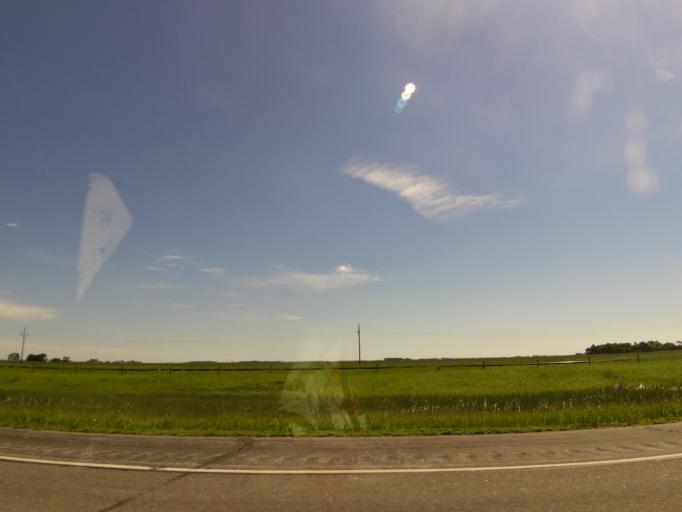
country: US
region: North Dakota
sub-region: Traill County
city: Hillsboro
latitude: 47.2185
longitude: -96.9961
